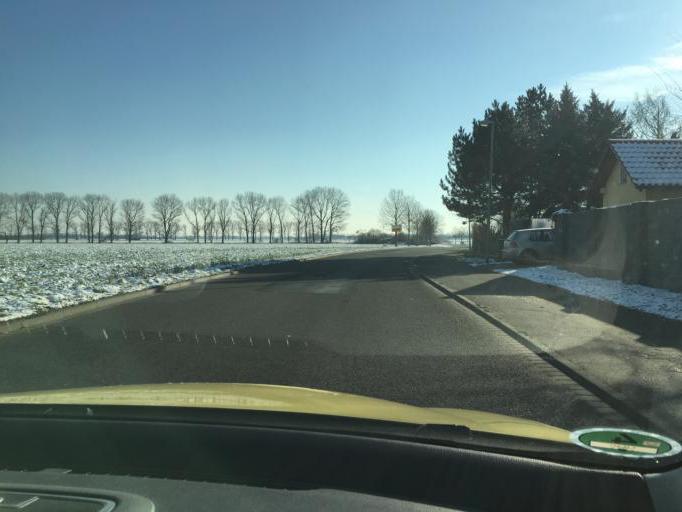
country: DE
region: Saxony
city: Borsdorf
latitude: 51.3201
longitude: 12.4956
